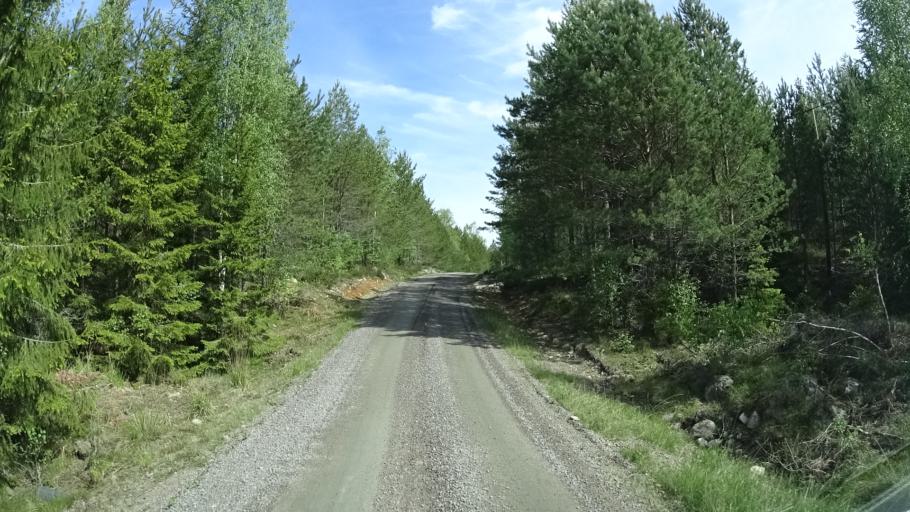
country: SE
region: OEstergoetland
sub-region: Finspangs Kommun
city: Finspang
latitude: 58.7729
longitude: 15.8523
